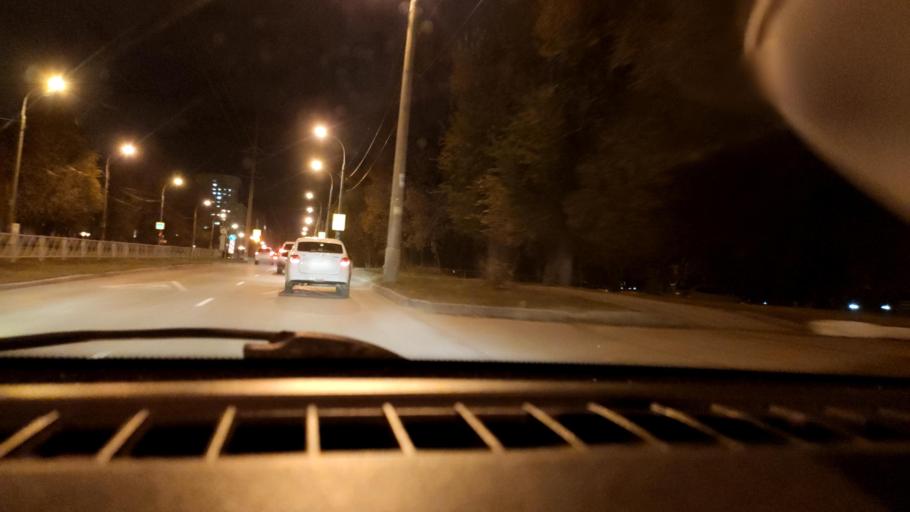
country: RU
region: Samara
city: Samara
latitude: 53.2023
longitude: 50.2140
